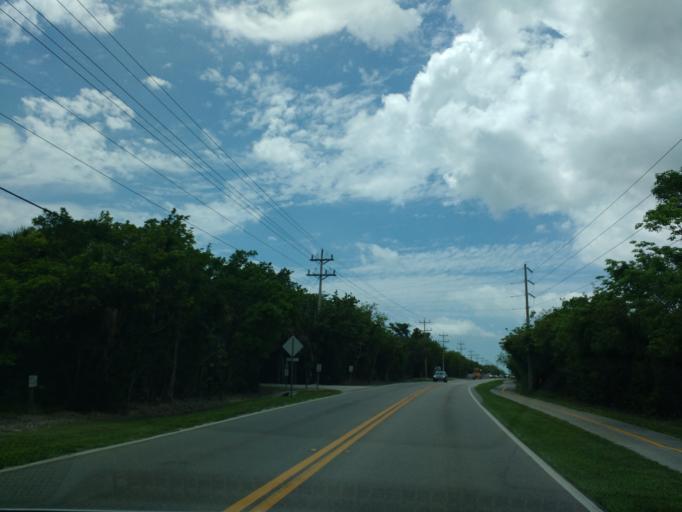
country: US
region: Florida
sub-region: Lee County
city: Saint James City
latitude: 26.4429
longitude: -82.1091
